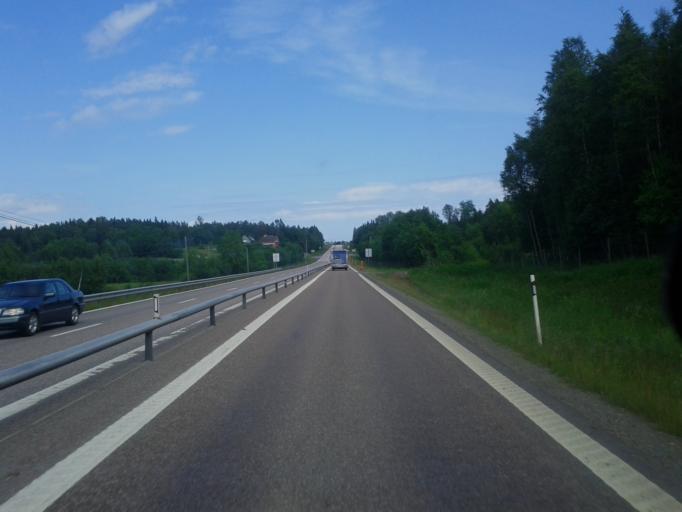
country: SE
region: Vaesternorrland
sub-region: OErnskoeldsviks Kommun
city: Husum
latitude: 63.3596
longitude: 19.1733
